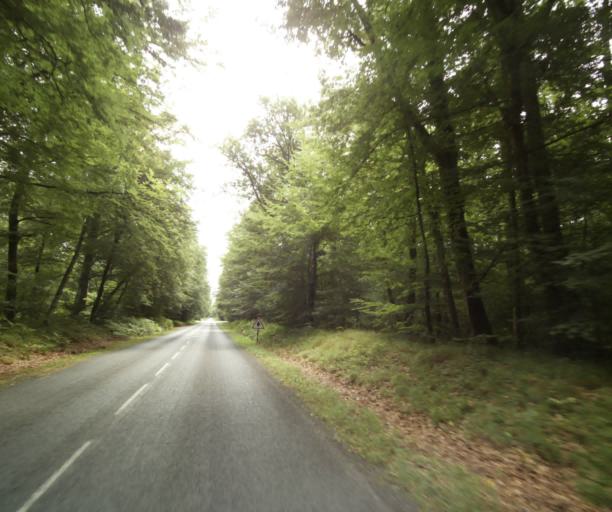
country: FR
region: Ile-de-France
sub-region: Departement de Seine-et-Marne
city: Bois-le-Roi
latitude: 48.4586
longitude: 2.7229
